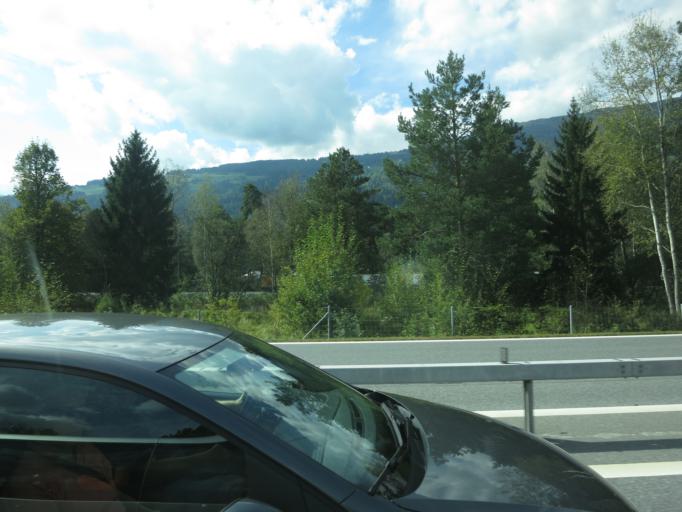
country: CH
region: Grisons
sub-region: Hinterrhein District
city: Cazis
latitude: 46.7402
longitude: 9.4343
